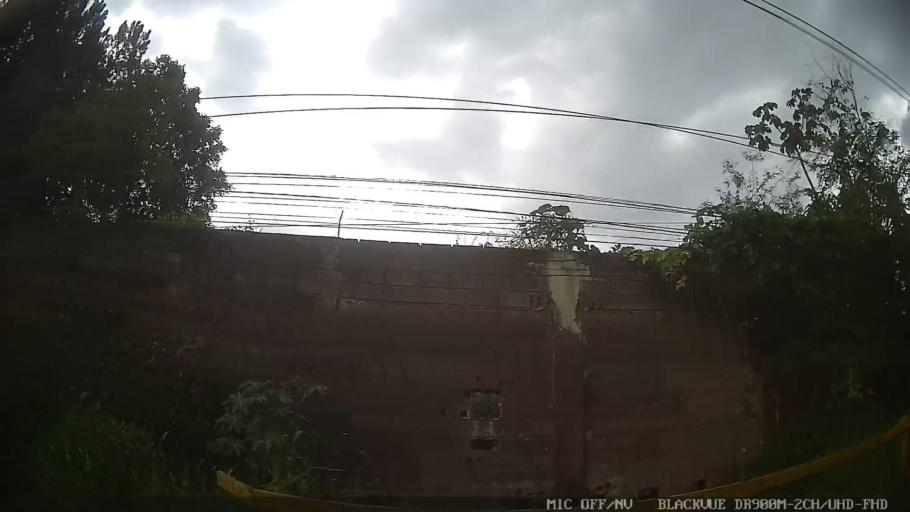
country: BR
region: Sao Paulo
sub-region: Suzano
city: Suzano
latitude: -23.5616
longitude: -46.3077
